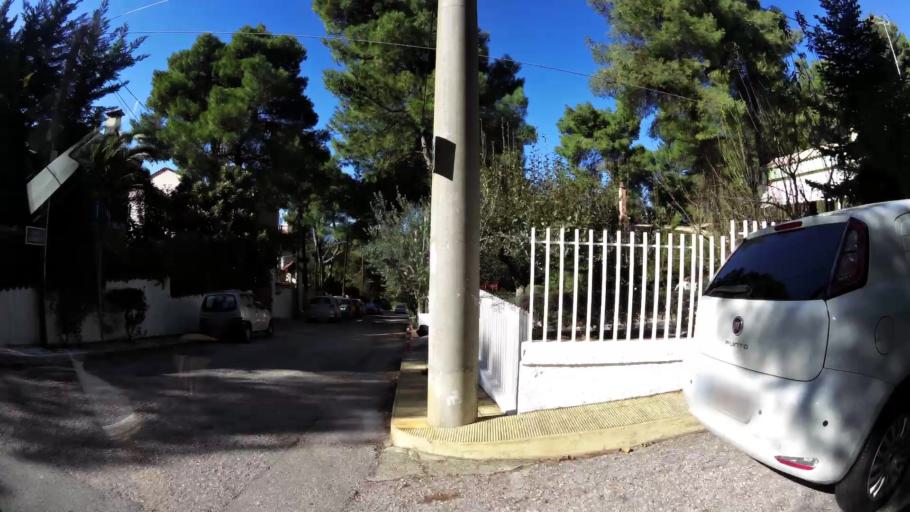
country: GR
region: Attica
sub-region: Nomarchia Athinas
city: Ekali
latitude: 38.1182
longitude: 23.8437
